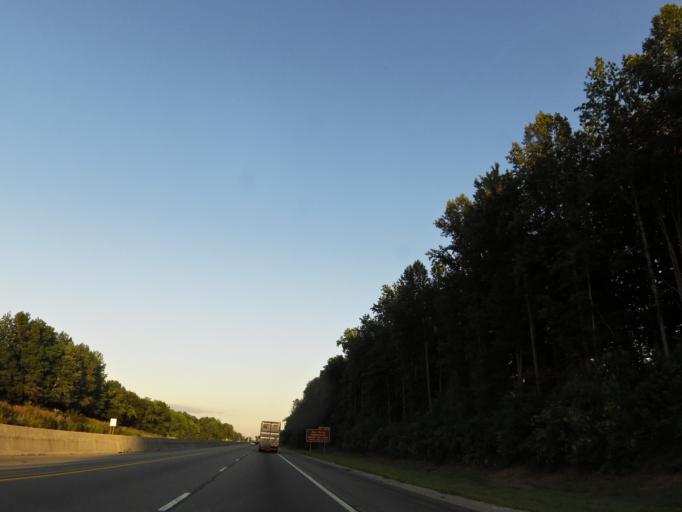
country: US
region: Tennessee
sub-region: Putnam County
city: Lafayette
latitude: 36.0945
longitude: -85.7347
